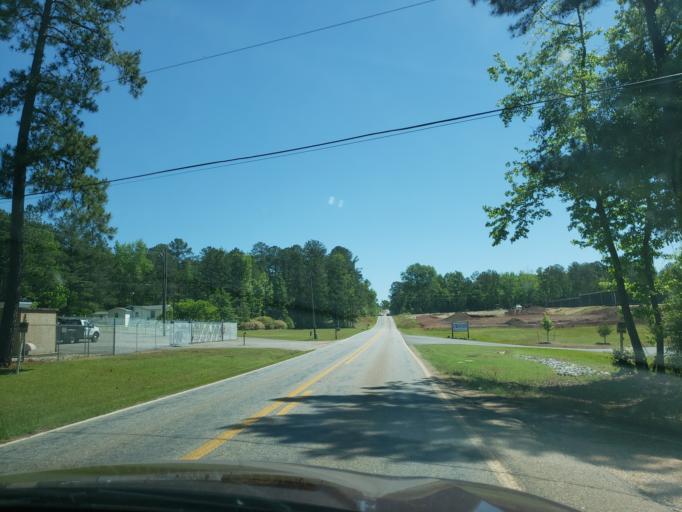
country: US
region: Alabama
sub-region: Tallapoosa County
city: Dadeville
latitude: 32.7078
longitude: -85.8001
